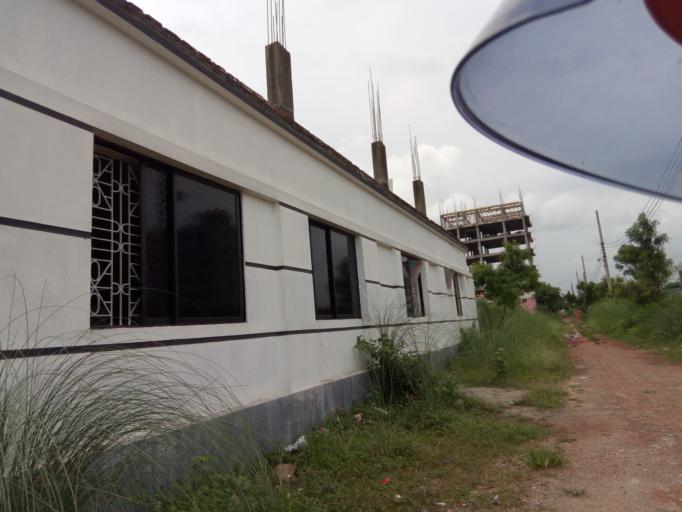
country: BD
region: Dhaka
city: Azimpur
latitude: 23.7499
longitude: 90.3457
